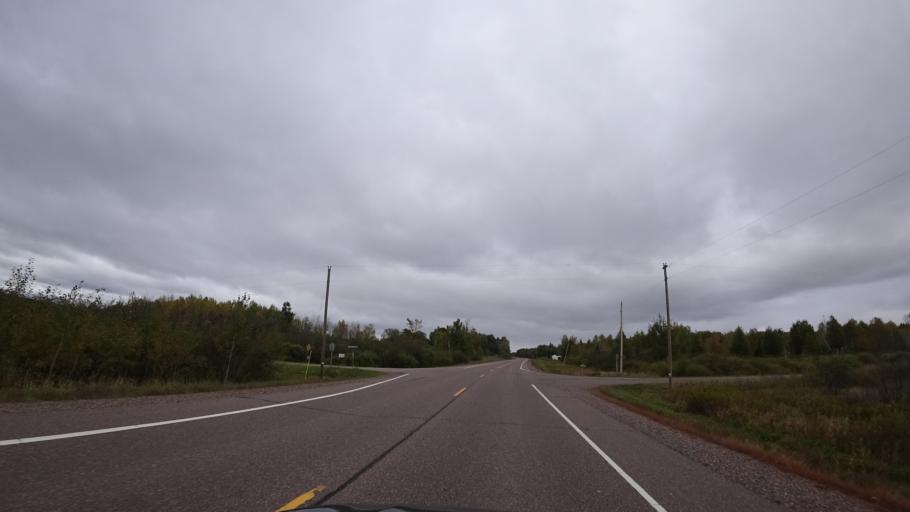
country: US
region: Wisconsin
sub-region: Rusk County
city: Ladysmith
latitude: 45.5520
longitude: -91.1120
